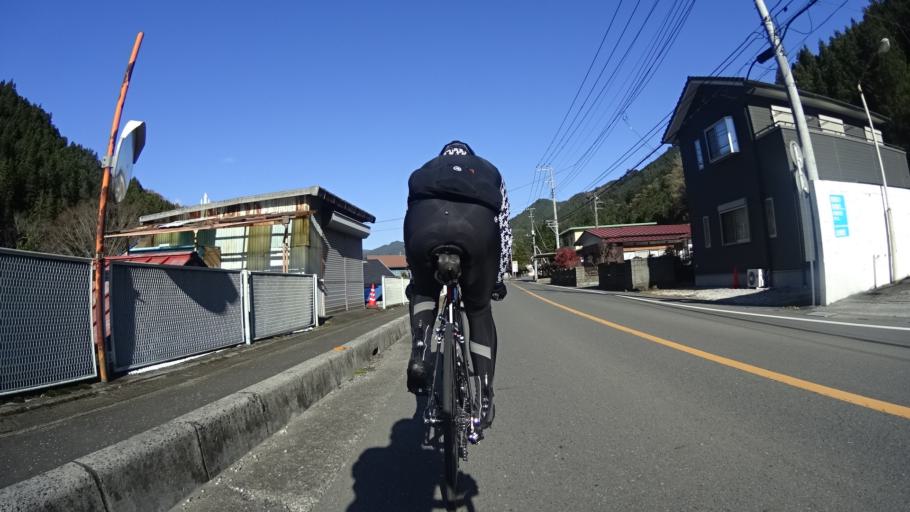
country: JP
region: Tokyo
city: Ome
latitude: 35.8763
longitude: 139.1860
